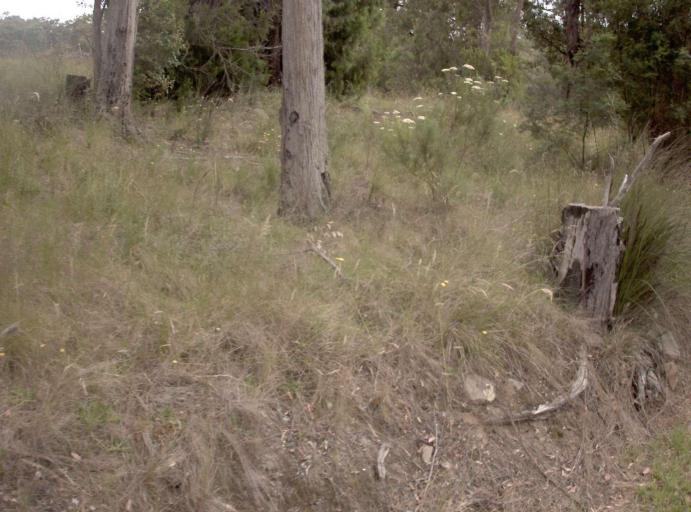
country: AU
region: Victoria
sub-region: East Gippsland
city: Bairnsdale
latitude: -37.7237
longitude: 147.5923
